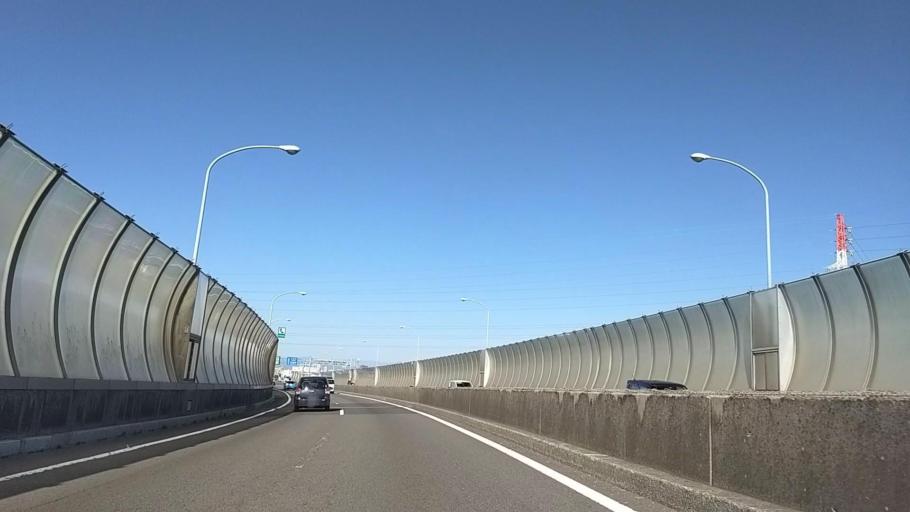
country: JP
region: Kanagawa
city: Minami-rinkan
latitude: 35.5020
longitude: 139.4901
